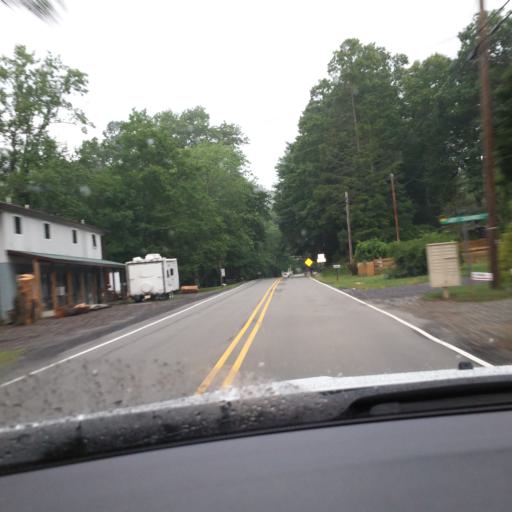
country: US
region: North Carolina
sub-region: Yancey County
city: Burnsville
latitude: 35.8095
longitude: -82.1989
